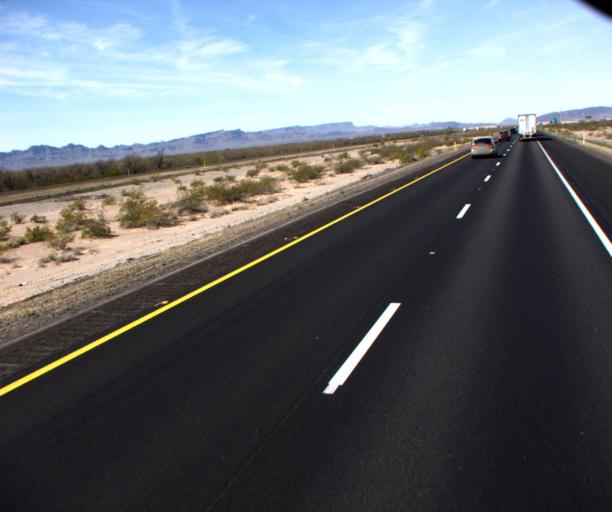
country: US
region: Arizona
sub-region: La Paz County
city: Salome
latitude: 33.6285
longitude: -113.7488
